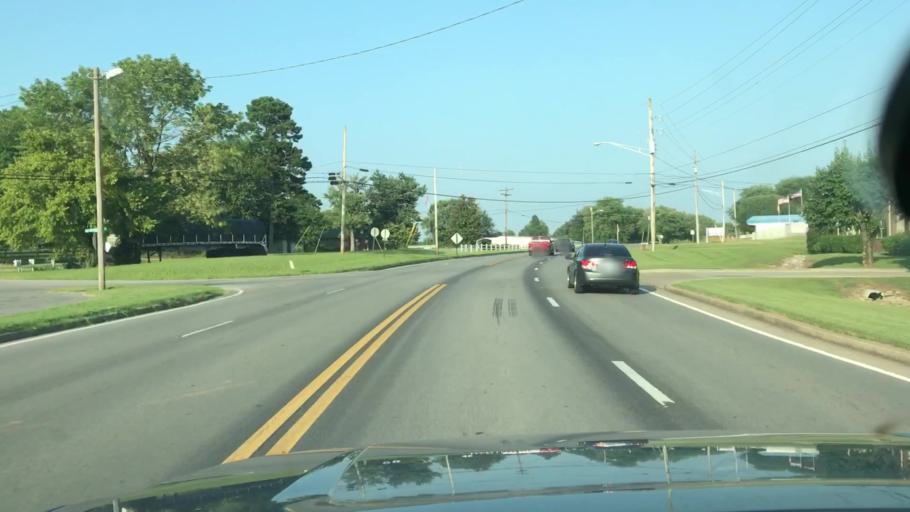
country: US
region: Tennessee
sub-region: Sumner County
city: Portland
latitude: 36.5778
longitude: -86.5008
